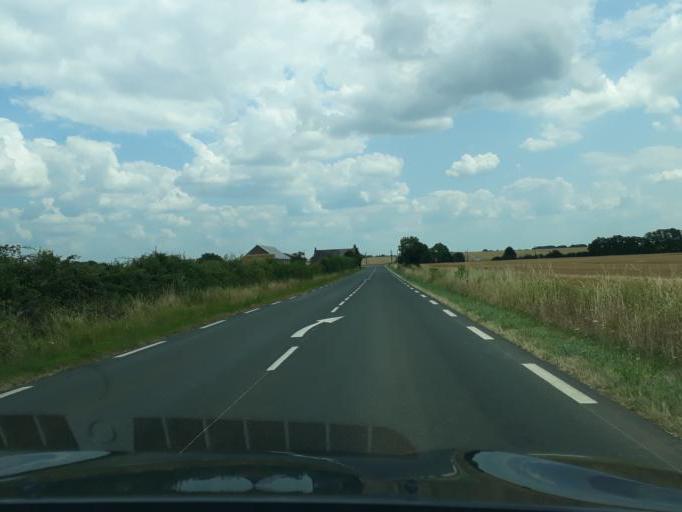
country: FR
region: Centre
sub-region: Departement du Cher
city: Avord
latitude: 47.0180
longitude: 2.7027
